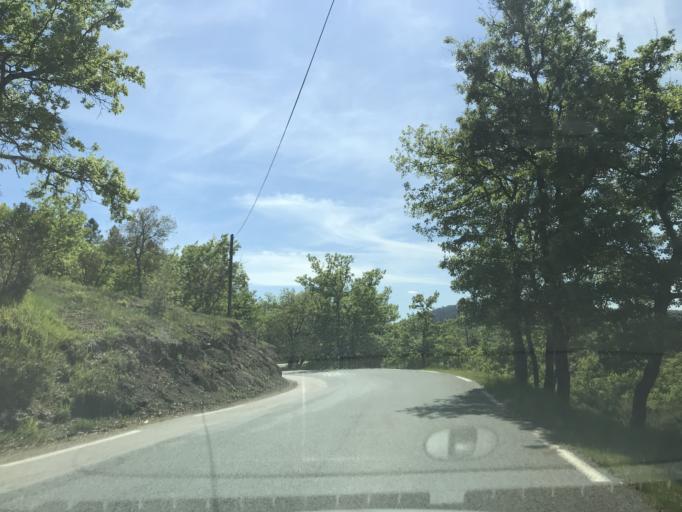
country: FR
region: Provence-Alpes-Cote d'Azur
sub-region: Departement du Var
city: Montauroux
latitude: 43.5843
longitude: 6.8160
